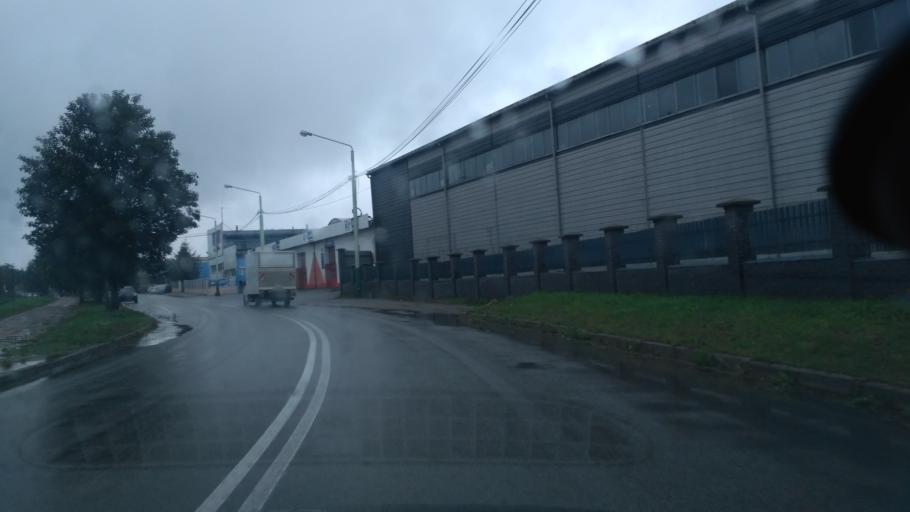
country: PL
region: Subcarpathian Voivodeship
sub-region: Powiat debicki
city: Debica
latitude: 50.0554
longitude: 21.3917
